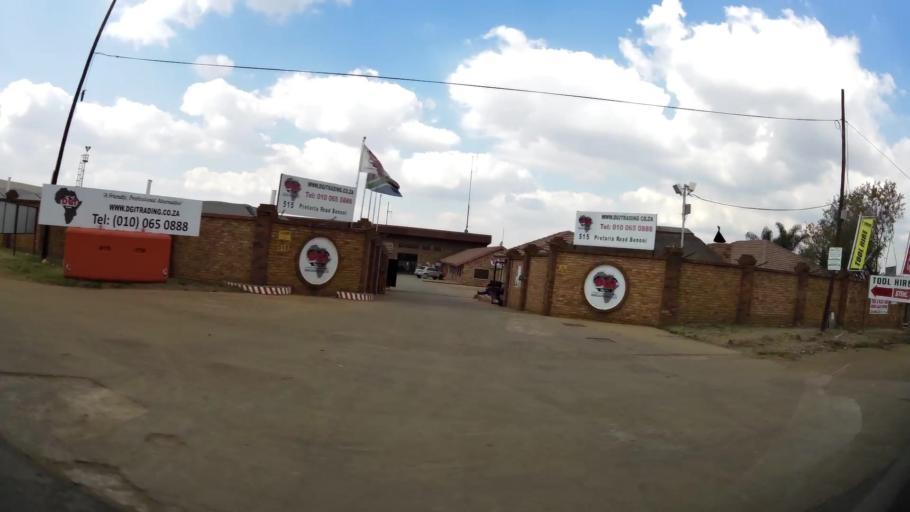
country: ZA
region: Gauteng
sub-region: Ekurhuleni Metropolitan Municipality
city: Benoni
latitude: -26.1283
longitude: 28.3549
